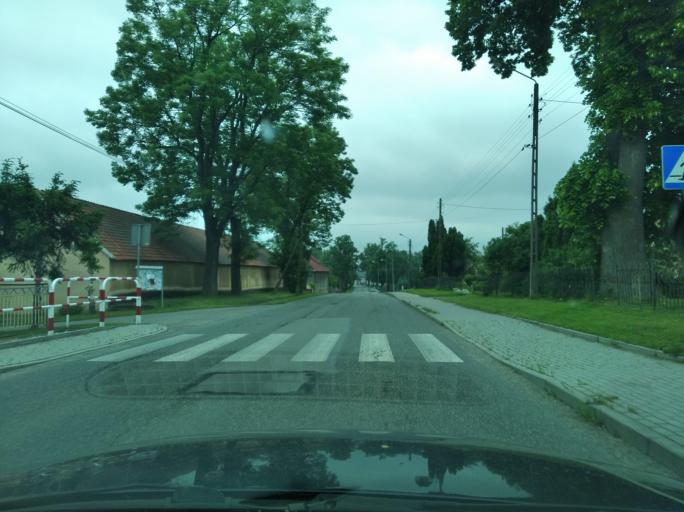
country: PL
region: Subcarpathian Voivodeship
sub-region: Powiat ropczycko-sedziszowski
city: Sedziszow Malopolski
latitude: 50.0550
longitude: 21.6871
